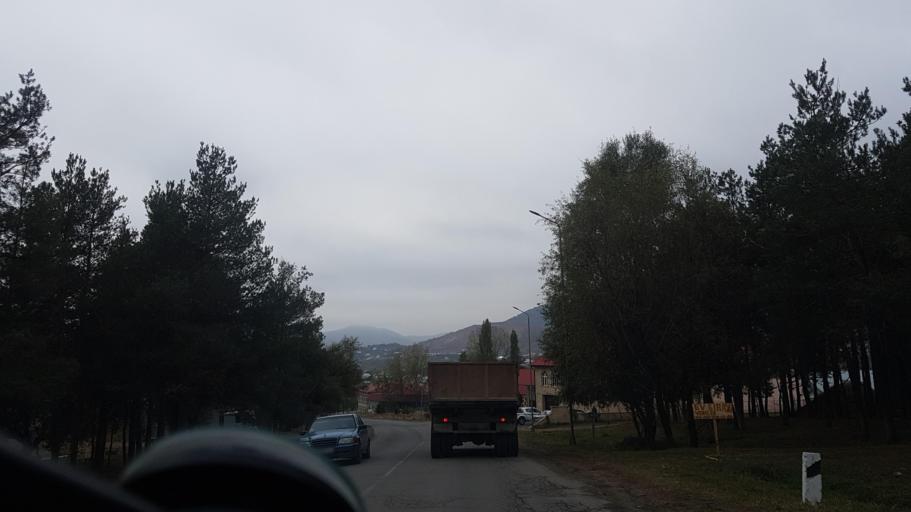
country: AZ
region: Gadabay Rayon
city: Ariqdam
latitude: 40.6014
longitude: 45.8110
